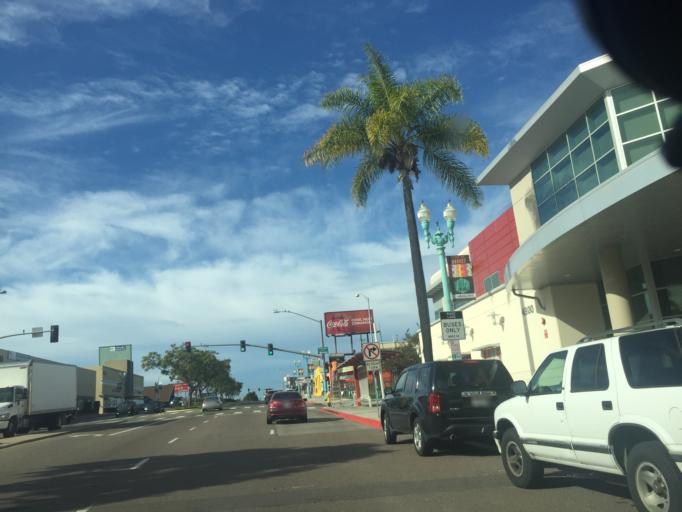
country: US
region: California
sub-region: San Diego County
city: San Diego
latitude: 32.7552
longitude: -117.1013
